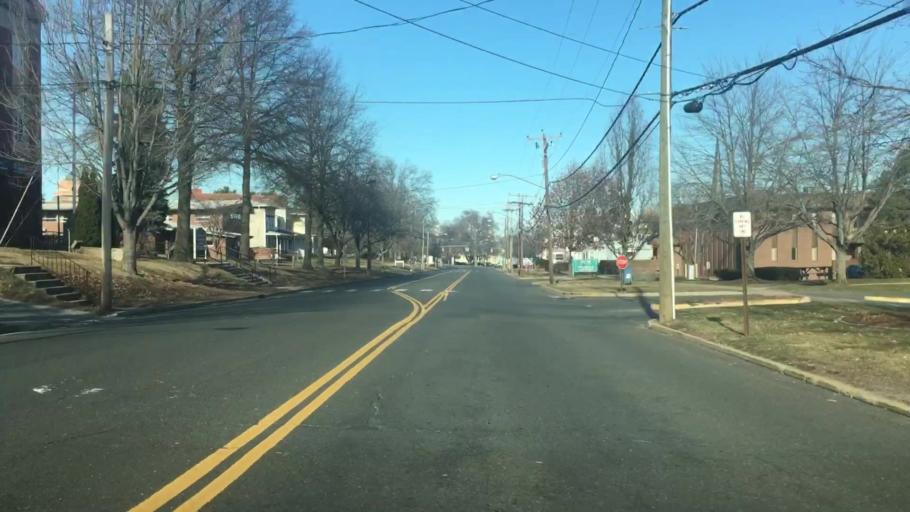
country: US
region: Connecticut
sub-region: Middlesex County
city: Middletown
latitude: 41.5534
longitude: -72.6492
